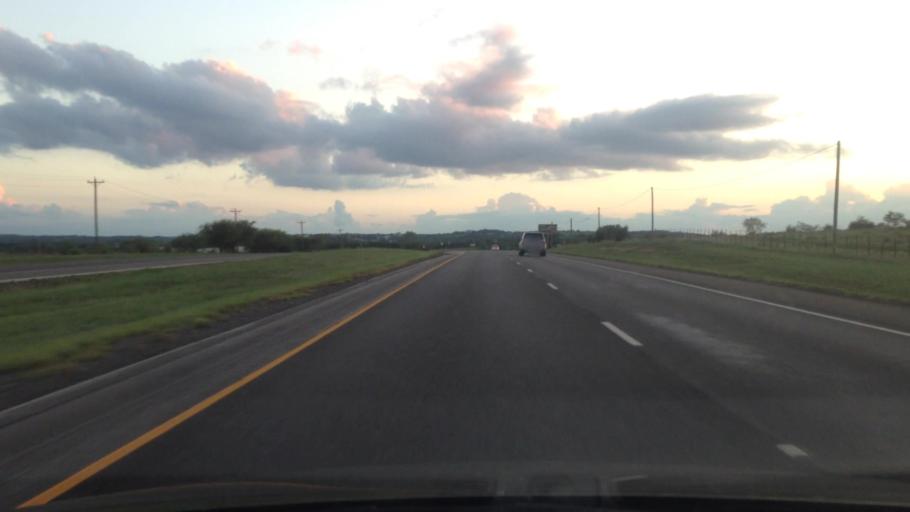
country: US
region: Texas
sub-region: Parker County
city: Aledo
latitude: 32.5909
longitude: -97.5873
